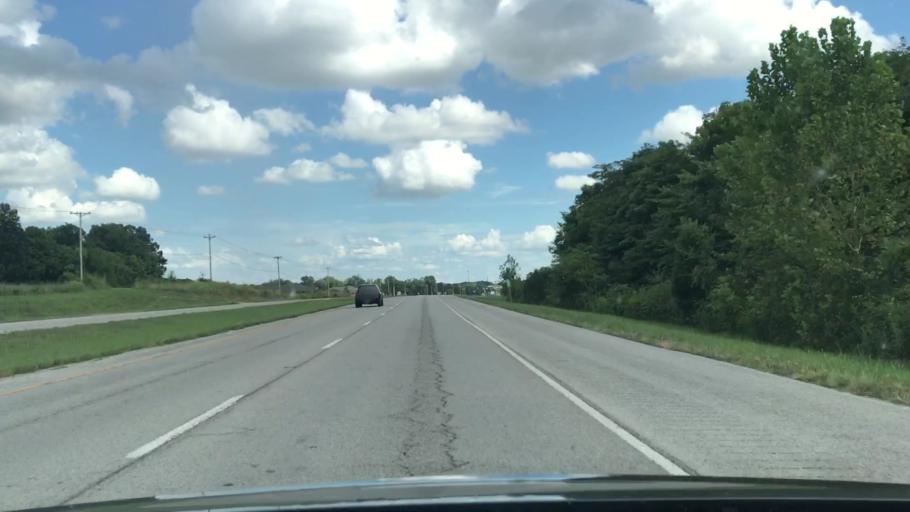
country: US
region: Kentucky
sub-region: Christian County
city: Hopkinsville
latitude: 36.8316
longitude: -87.5231
